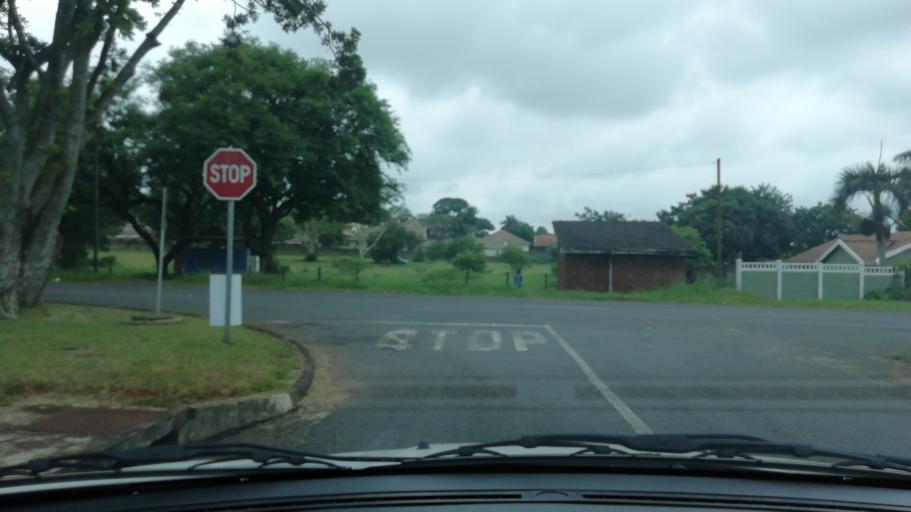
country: ZA
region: KwaZulu-Natal
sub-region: uThungulu District Municipality
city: Empangeni
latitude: -28.7648
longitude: 31.9027
